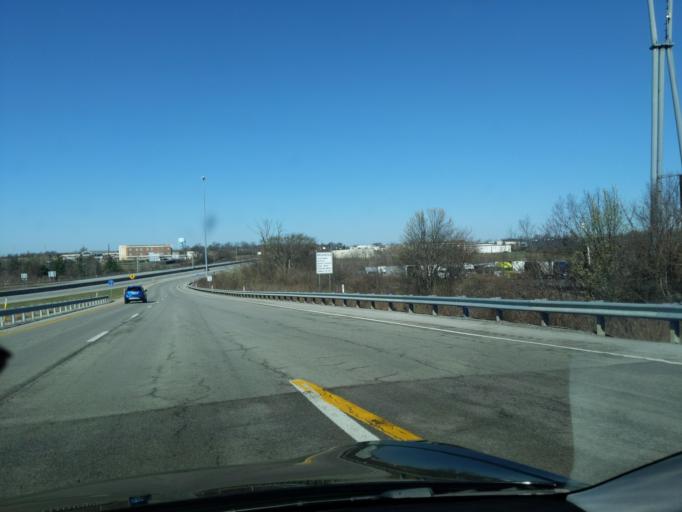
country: US
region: Kentucky
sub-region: Clark County
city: Winchester
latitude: 38.0128
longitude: -84.2093
